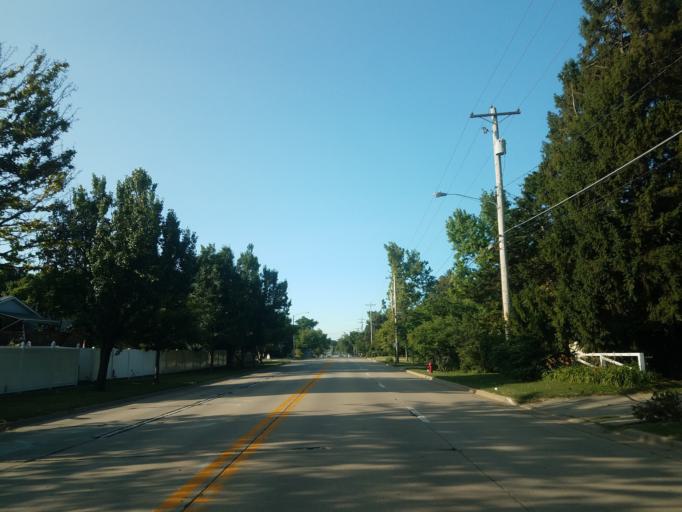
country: US
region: Illinois
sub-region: McLean County
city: Normal
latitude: 40.5302
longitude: -88.9832
